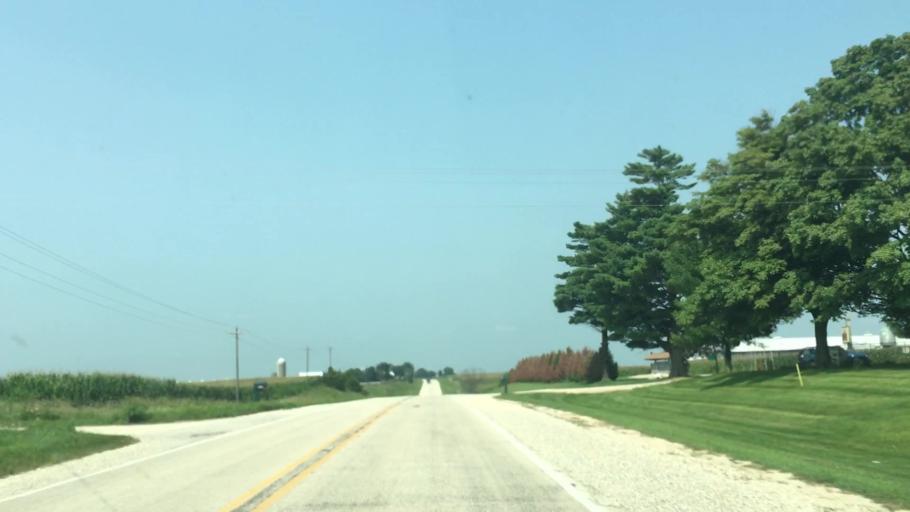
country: US
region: Iowa
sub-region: Fayette County
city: West Union
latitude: 43.0081
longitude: -91.8243
